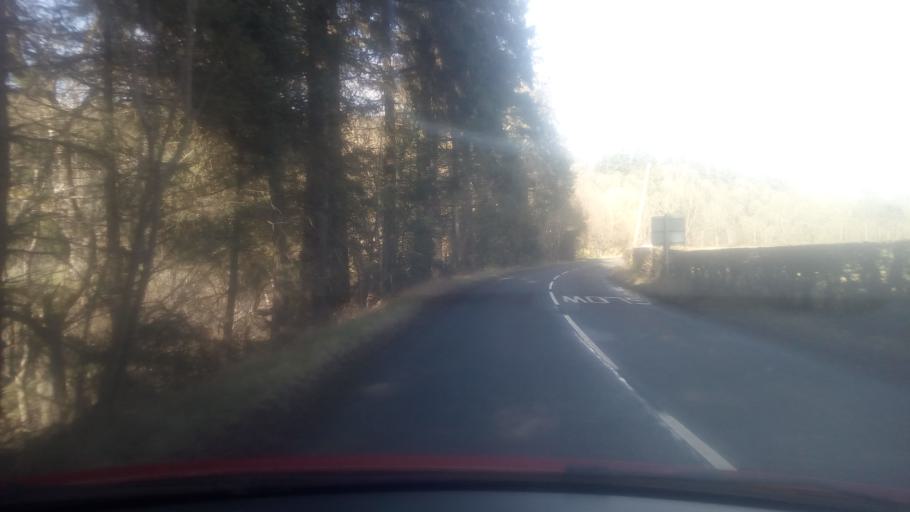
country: GB
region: Scotland
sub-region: The Scottish Borders
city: Selkirk
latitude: 55.5868
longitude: -2.8673
